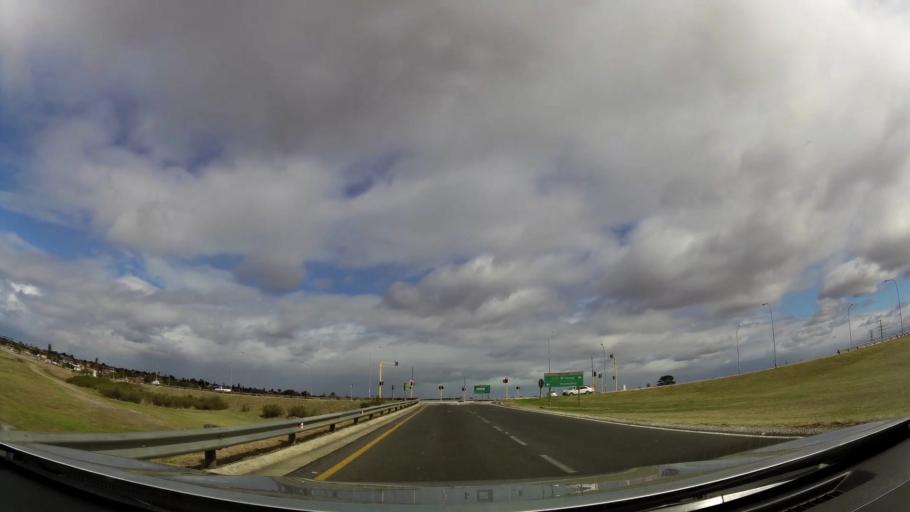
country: ZA
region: Western Cape
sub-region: Eden District Municipality
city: George
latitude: -33.9990
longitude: 22.4462
